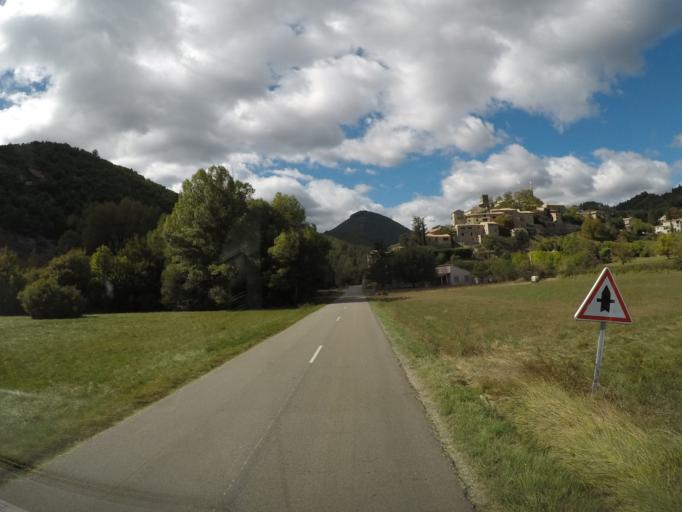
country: FR
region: Provence-Alpes-Cote d'Azur
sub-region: Departement du Vaucluse
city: Sault
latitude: 44.1671
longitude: 5.4234
